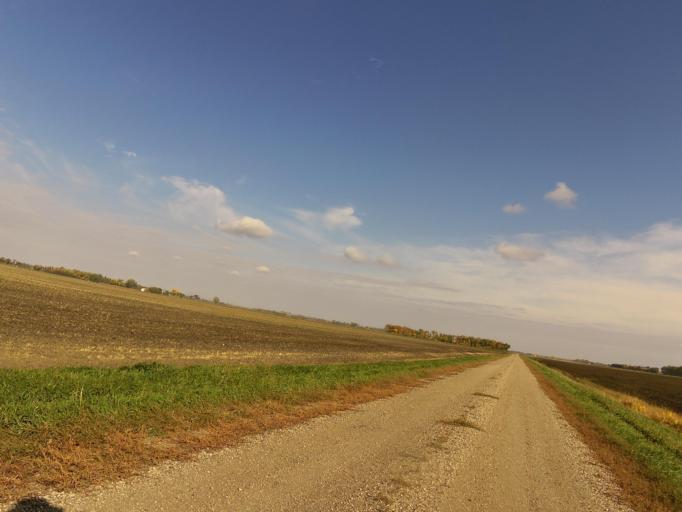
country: US
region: North Dakota
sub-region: Walsh County
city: Grafton
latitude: 48.3974
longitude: -97.2220
